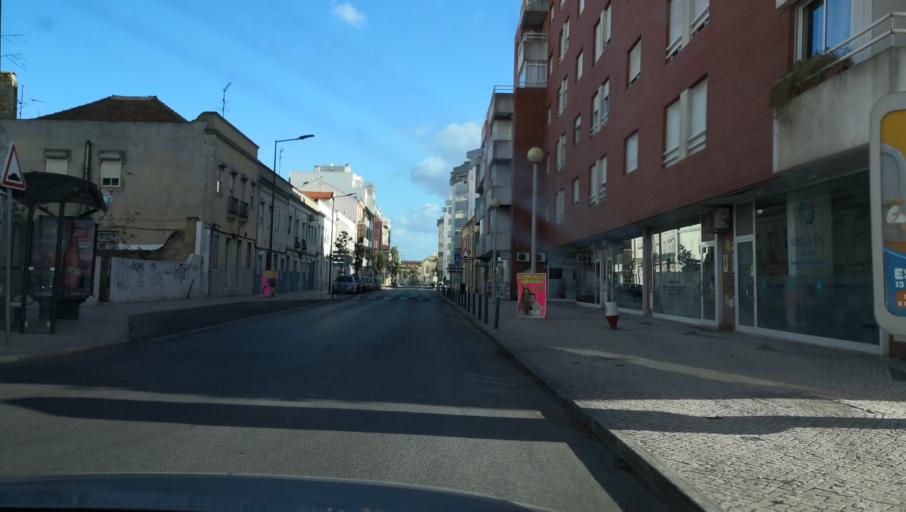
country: PT
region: Setubal
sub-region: Barreiro
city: Barreiro
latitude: 38.6595
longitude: -9.0814
